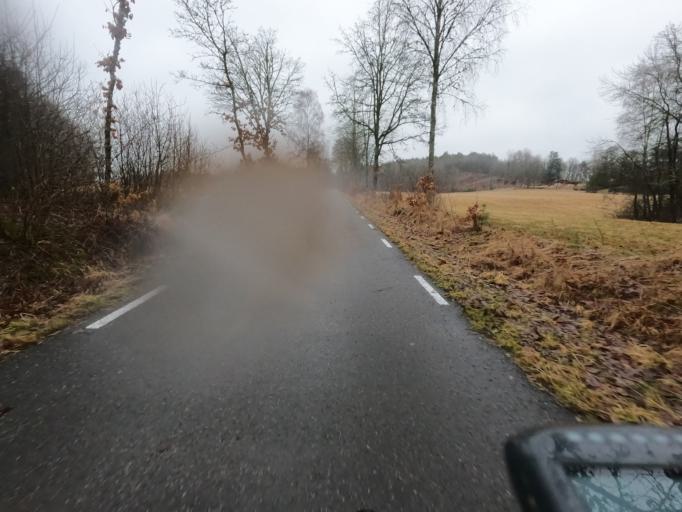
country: SE
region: Halland
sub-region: Halmstads Kommun
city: Aled
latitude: 56.6986
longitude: 13.0188
